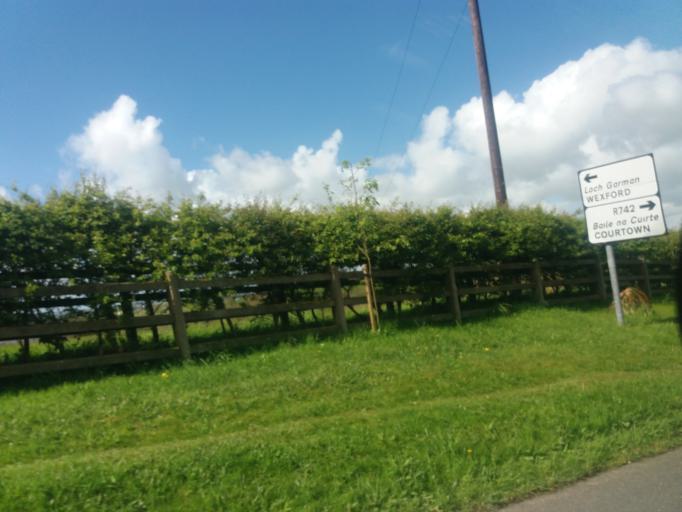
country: IE
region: Leinster
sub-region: Loch Garman
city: Castlebridge
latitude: 52.3907
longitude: -6.3840
